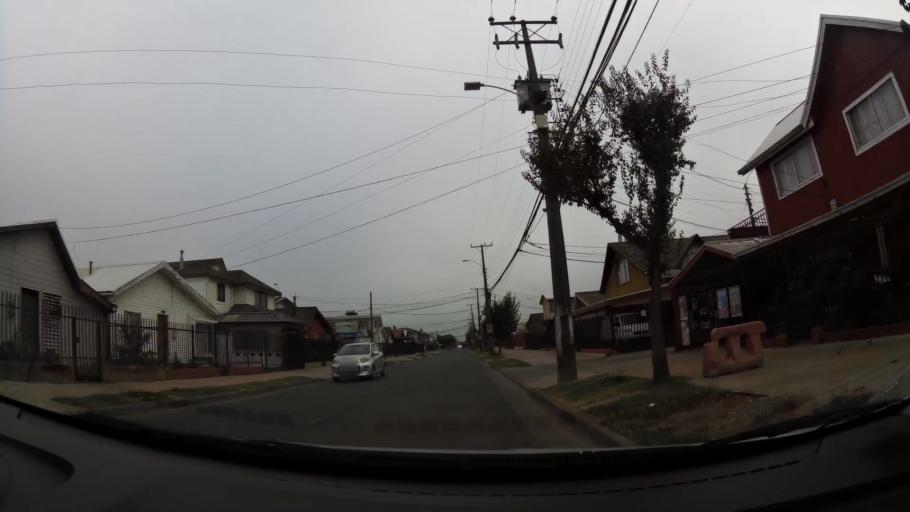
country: CL
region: Biobio
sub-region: Provincia de Concepcion
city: Concepcion
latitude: -36.7947
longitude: -73.0814
